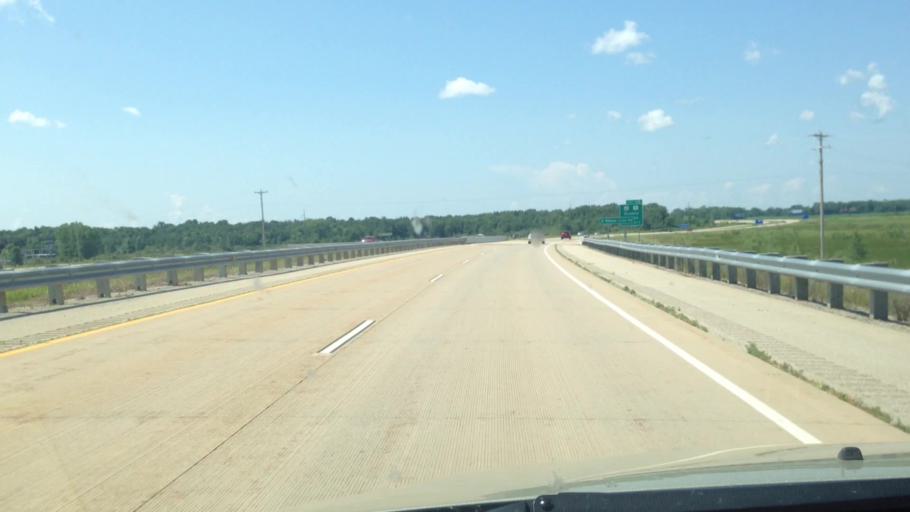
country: US
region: Wisconsin
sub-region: Oconto County
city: Oconto
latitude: 44.9068
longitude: -87.8840
